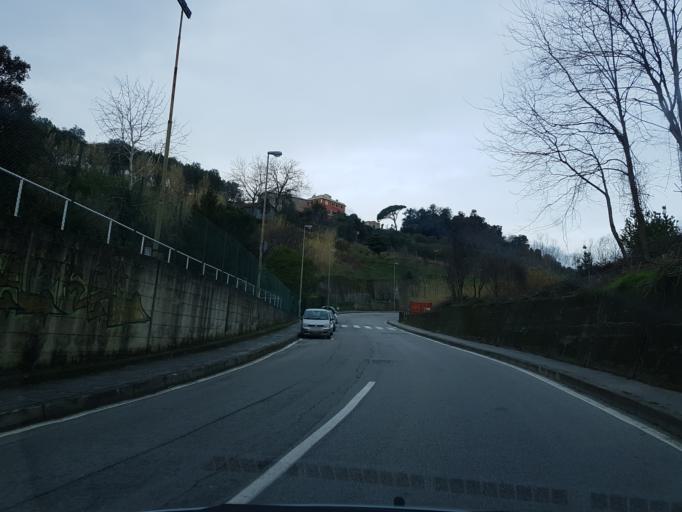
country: IT
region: Liguria
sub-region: Provincia di Genova
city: Mele
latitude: 44.4303
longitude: 8.8008
